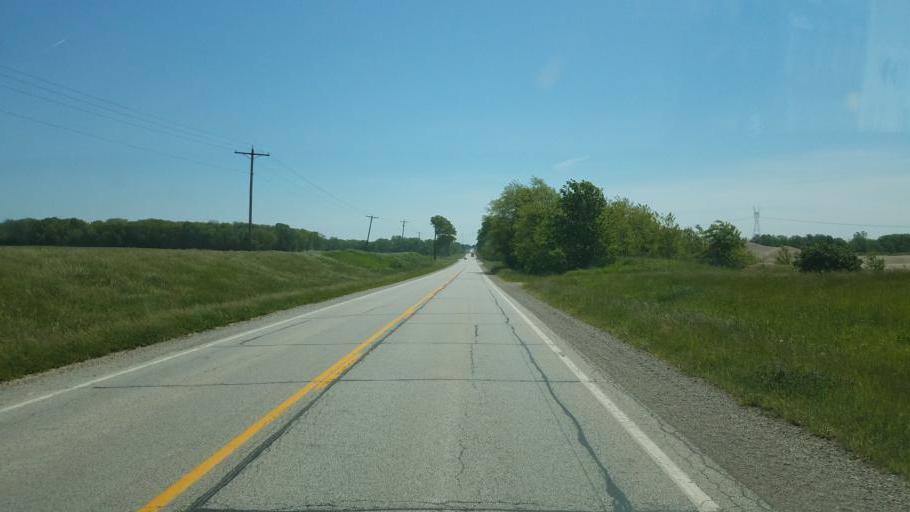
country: US
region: Illinois
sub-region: McLean County
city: Heyworth
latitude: 40.3122
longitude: -89.0251
